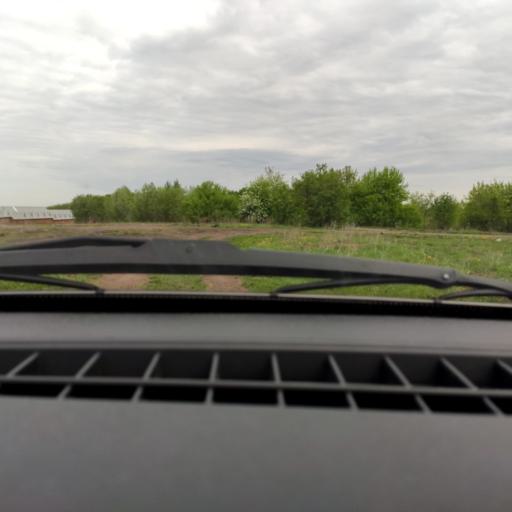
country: RU
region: Bashkortostan
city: Avdon
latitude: 54.6991
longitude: 55.8084
